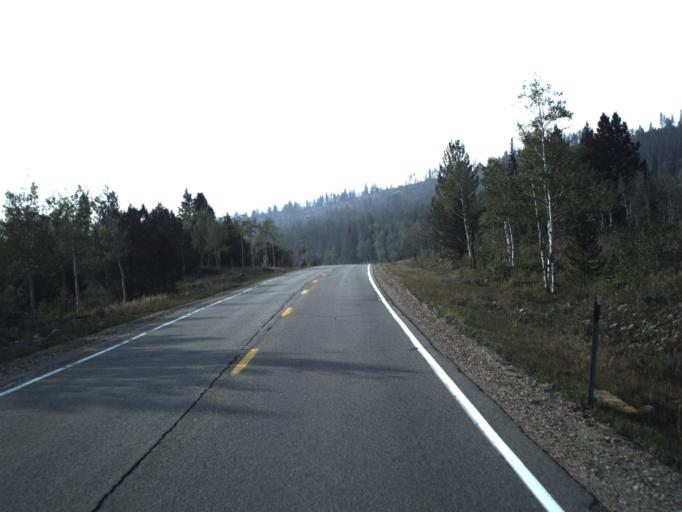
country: US
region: Utah
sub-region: Summit County
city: Francis
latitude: 40.5914
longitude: -111.0694
